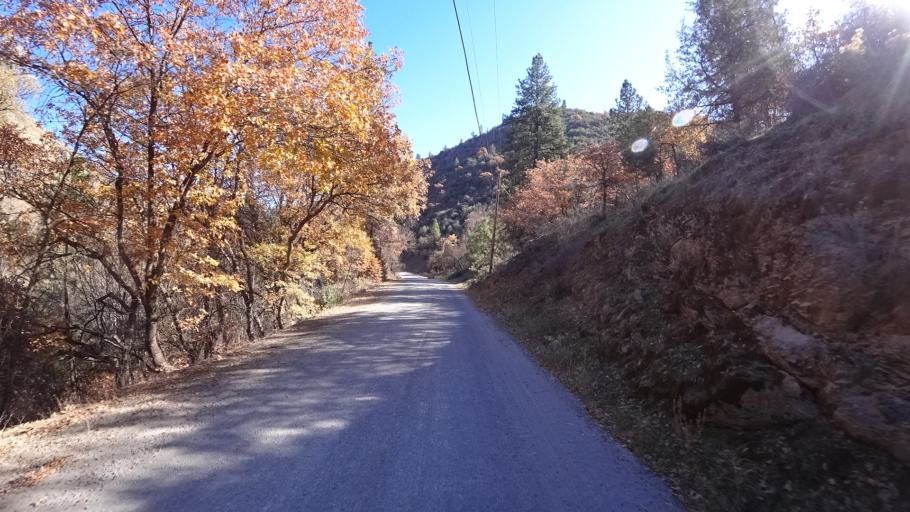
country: US
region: California
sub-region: Siskiyou County
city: Yreka
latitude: 41.8314
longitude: -122.6319
